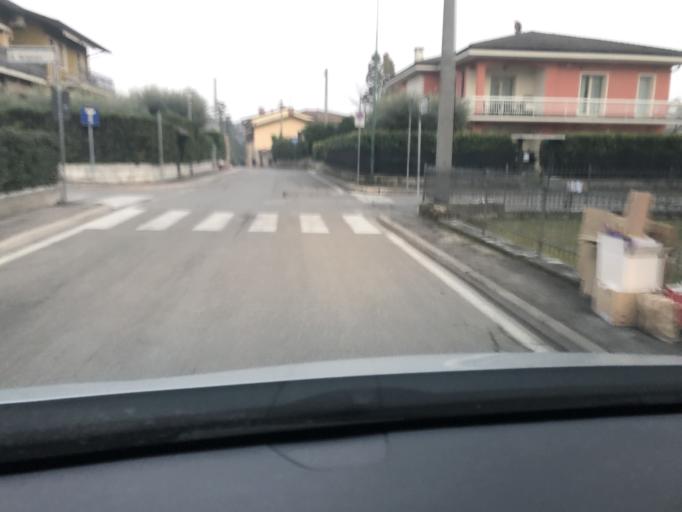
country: IT
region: Veneto
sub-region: Provincia di Verona
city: Sommacampagna
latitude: 45.4066
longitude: 10.8391
